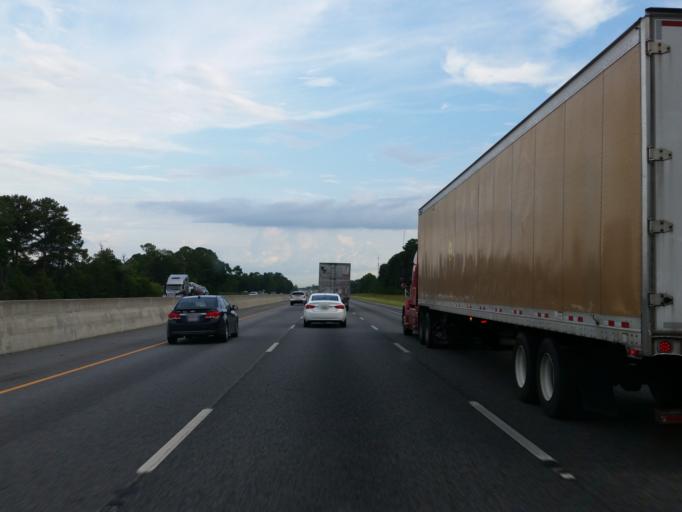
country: US
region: Georgia
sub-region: Lowndes County
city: Hahira
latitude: 31.0137
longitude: -83.3942
